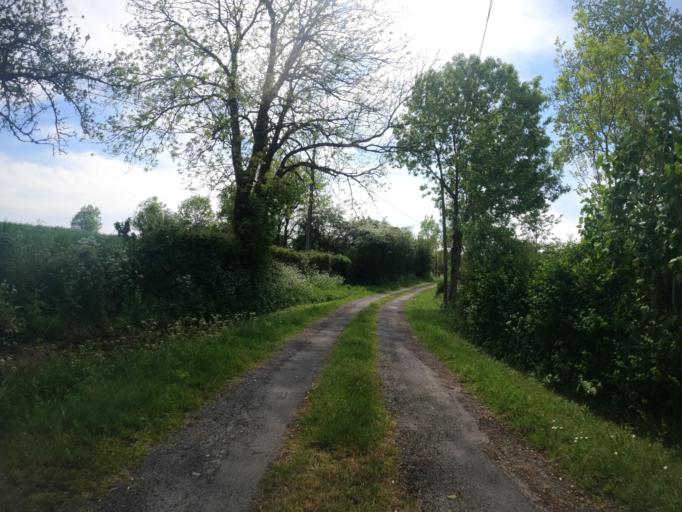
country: FR
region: Poitou-Charentes
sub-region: Departement des Deux-Sevres
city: La Chapelle-Saint-Laurent
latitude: 46.6568
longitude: -0.5149
